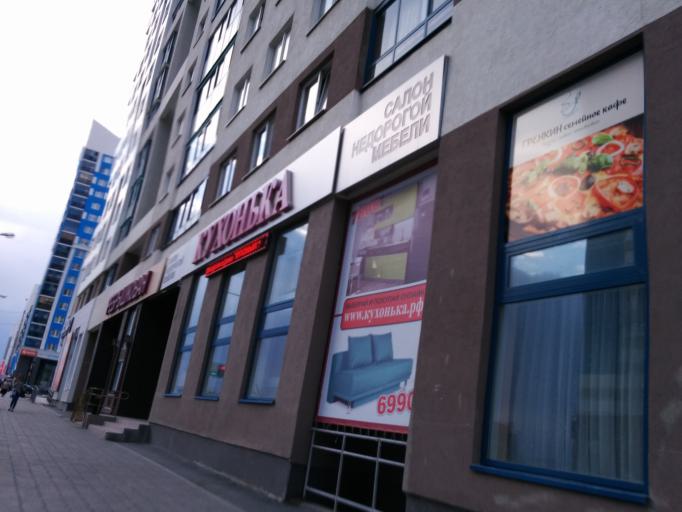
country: RU
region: Sverdlovsk
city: Shirokaya Rechka
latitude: 56.7890
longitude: 60.5163
